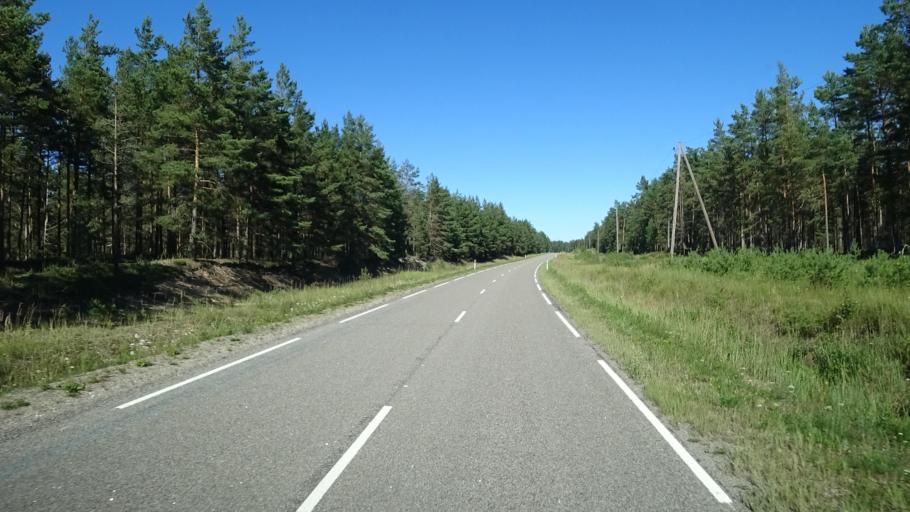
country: LV
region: Dundaga
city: Dundaga
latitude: 57.6794
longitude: 22.3516
